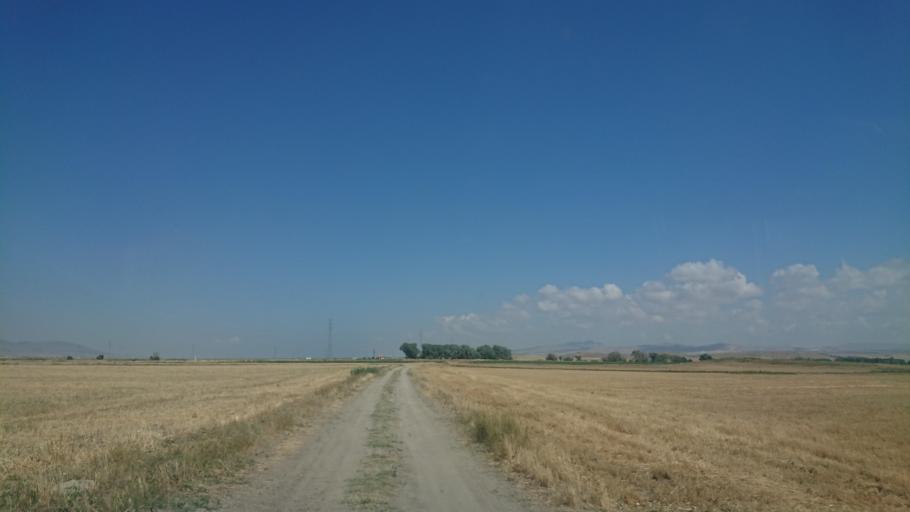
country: TR
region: Aksaray
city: Sariyahsi
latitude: 38.9924
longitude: 33.8975
